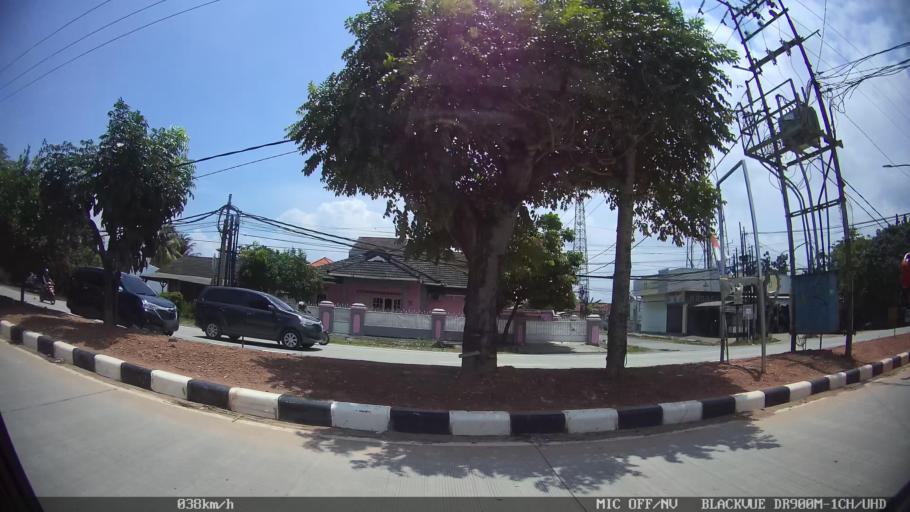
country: ID
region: Lampung
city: Kedaton
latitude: -5.3652
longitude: 105.3016
